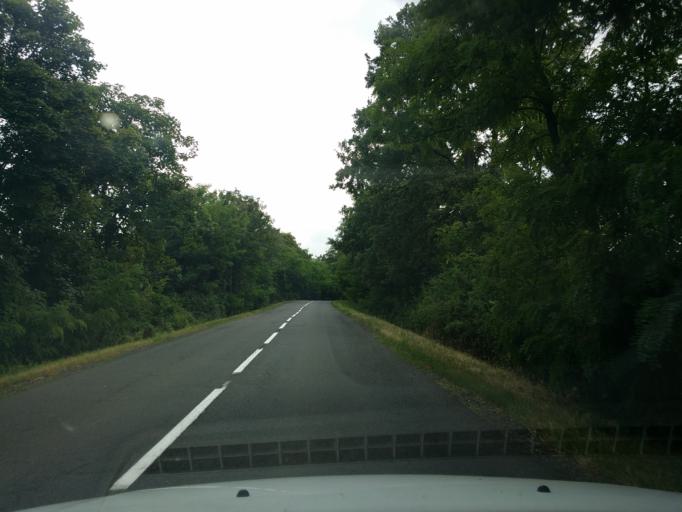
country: HU
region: Nograd
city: Bercel
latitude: 47.9351
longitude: 19.3684
